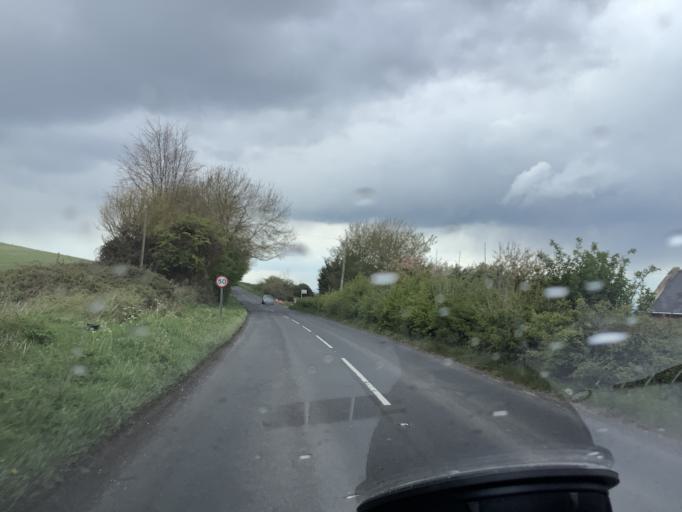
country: GB
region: England
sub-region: Wiltshire
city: Bratton
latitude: 51.2678
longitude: -2.1463
